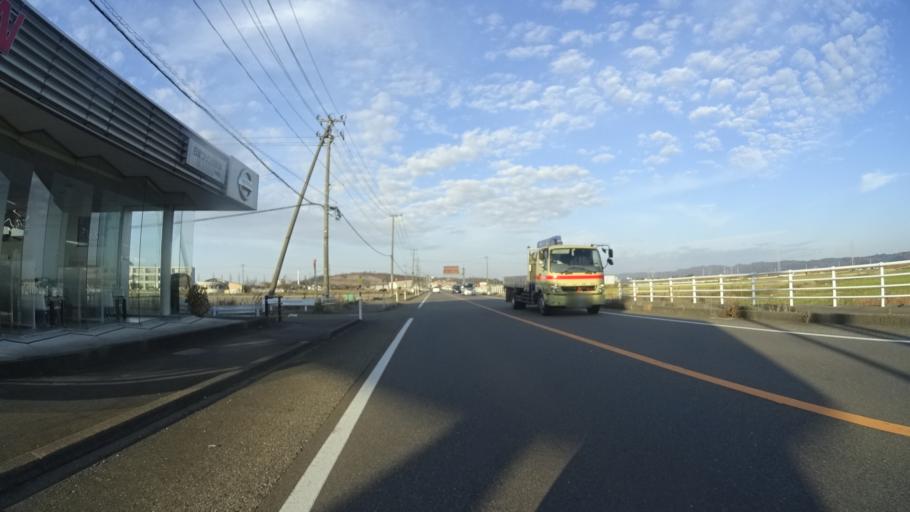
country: JP
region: Niigata
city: Kashiwazaki
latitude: 37.3810
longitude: 138.5815
